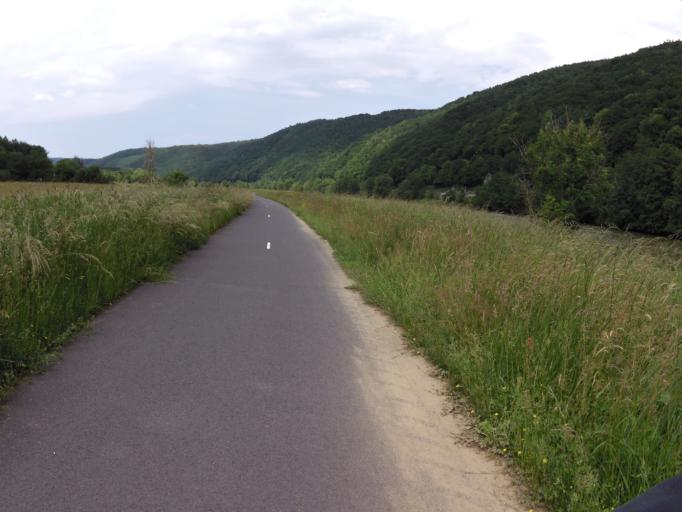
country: FR
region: Champagne-Ardenne
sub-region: Departement des Ardennes
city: Neufmanil
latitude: 49.8356
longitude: 4.7803
